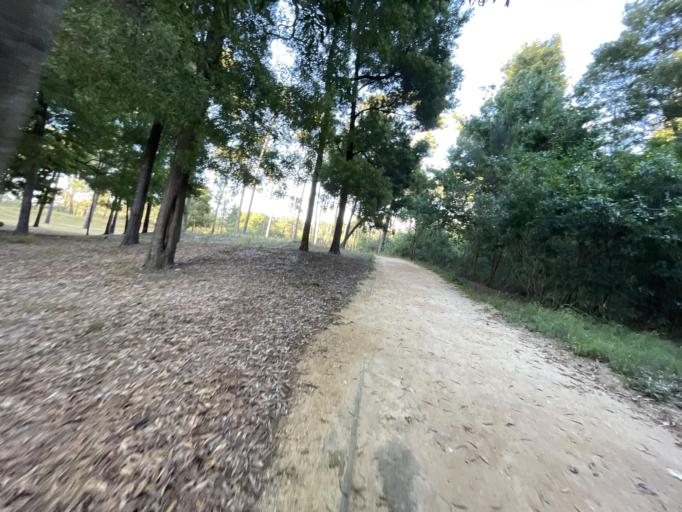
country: PT
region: Aveiro
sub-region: Ovar
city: Esmoriz
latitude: 40.9477
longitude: -8.6417
